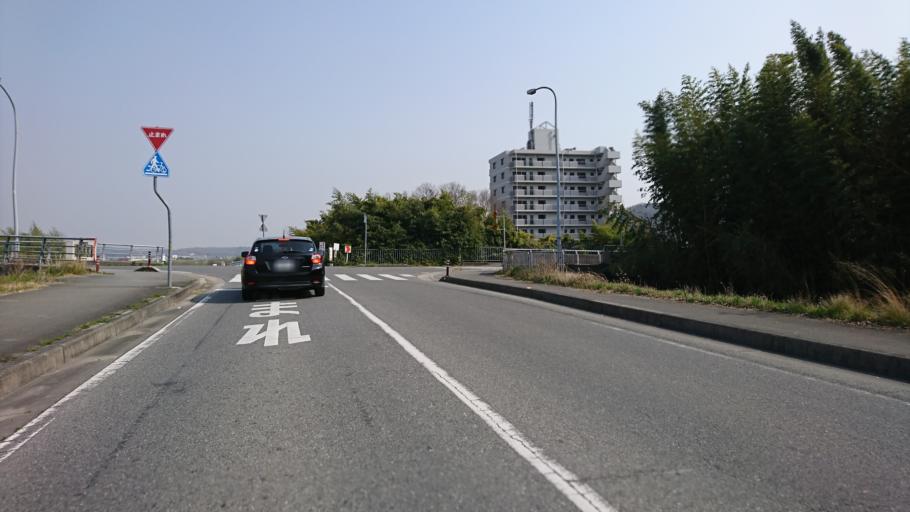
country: JP
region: Hyogo
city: Ono
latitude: 34.8362
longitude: 134.9195
